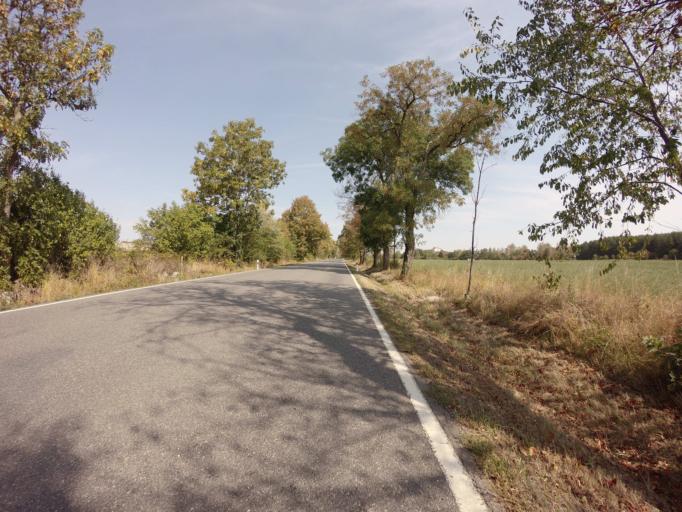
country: CZ
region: Central Bohemia
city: Petrovice
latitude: 49.6044
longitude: 14.3841
